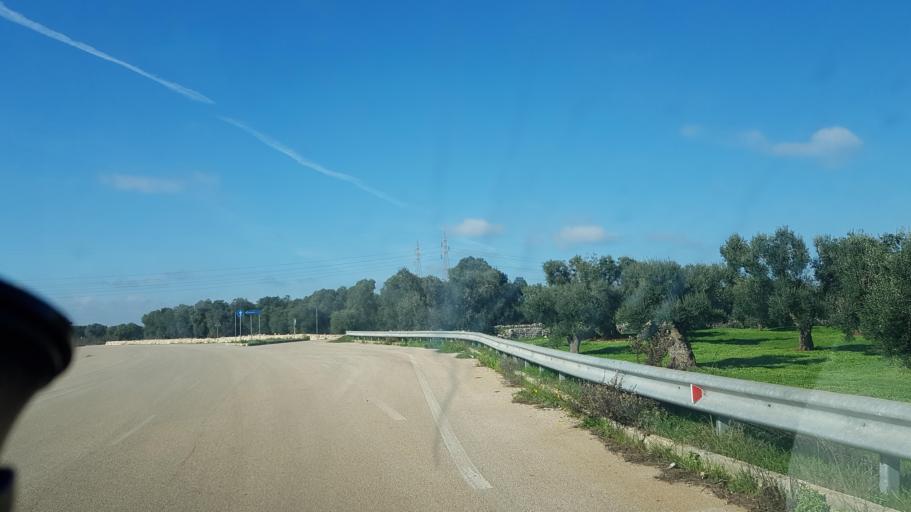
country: IT
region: Apulia
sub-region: Provincia di Brindisi
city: San Vito dei Normanni
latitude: 40.6742
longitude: 17.7081
